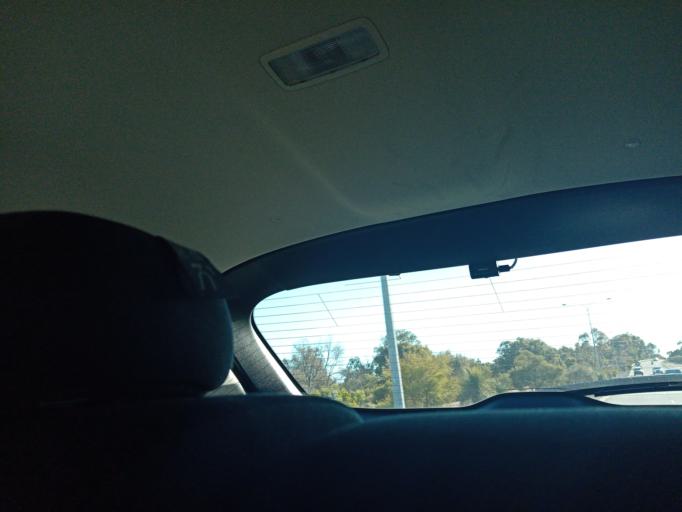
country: AU
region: Western Australia
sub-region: City of Cockburn
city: Yangebup
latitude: -32.1259
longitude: 115.8312
